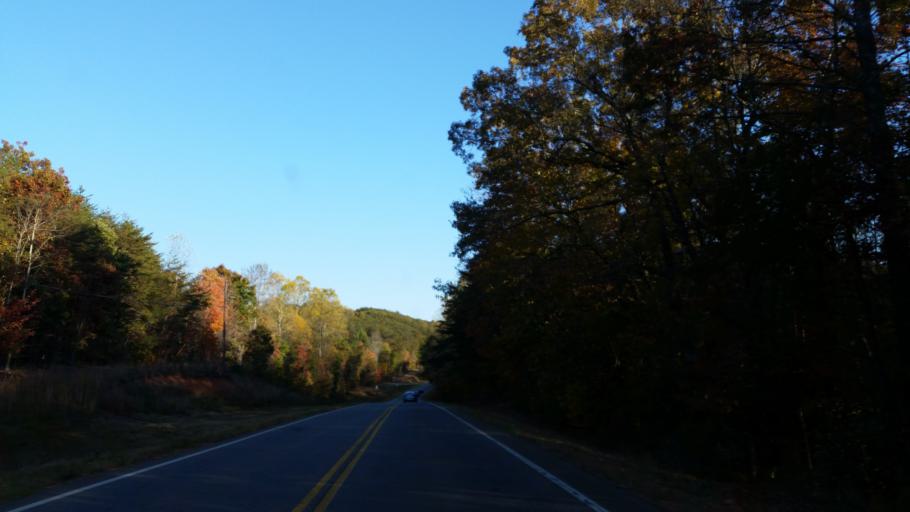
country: US
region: Georgia
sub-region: Pickens County
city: Jasper
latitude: 34.5481
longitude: -84.2814
